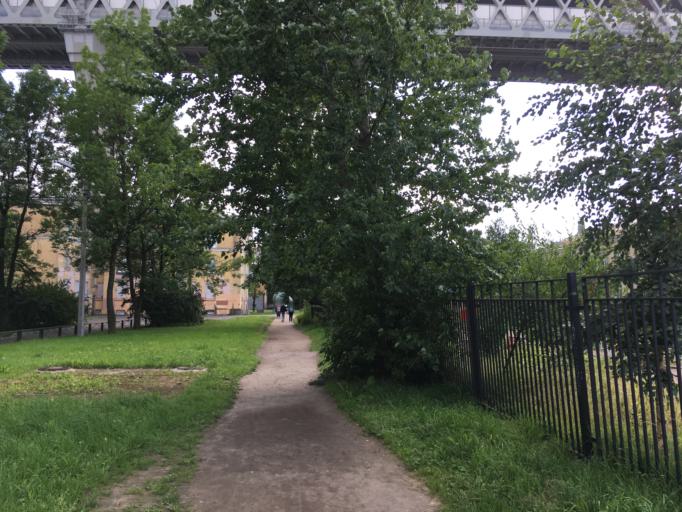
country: RU
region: St.-Petersburg
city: Vasyl'evsky Ostrov
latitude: 59.9024
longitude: 30.2200
